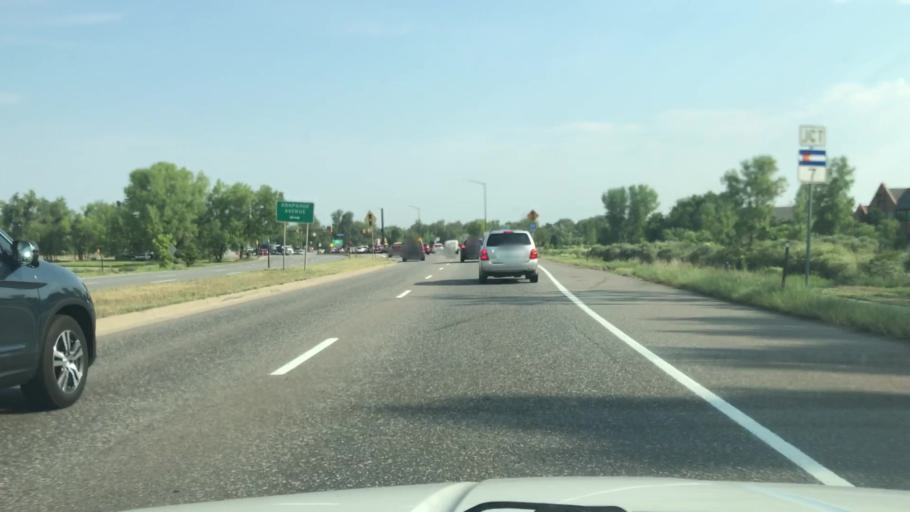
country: US
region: Colorado
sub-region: Boulder County
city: Boulder
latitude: 40.0123
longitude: -105.2403
